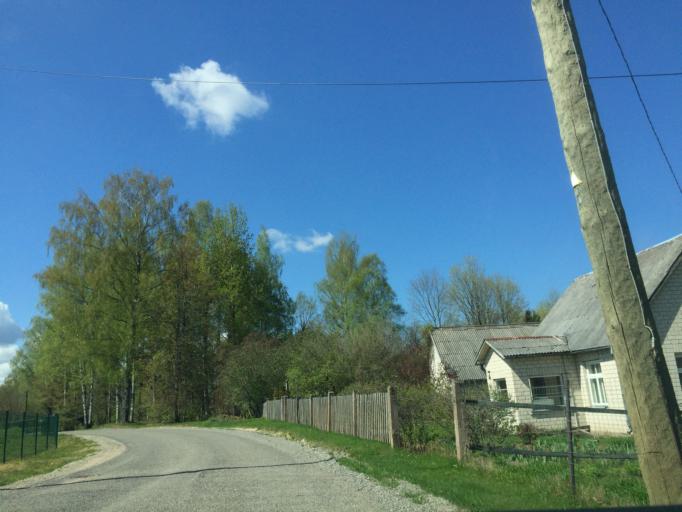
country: LV
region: Baldone
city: Baldone
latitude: 56.7411
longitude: 24.3732
